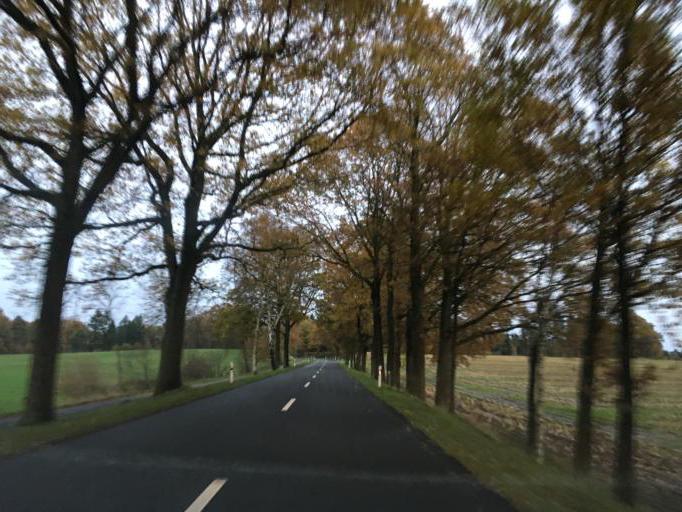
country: DE
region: Lower Saxony
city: Bispingen
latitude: 53.0995
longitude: 10.0076
